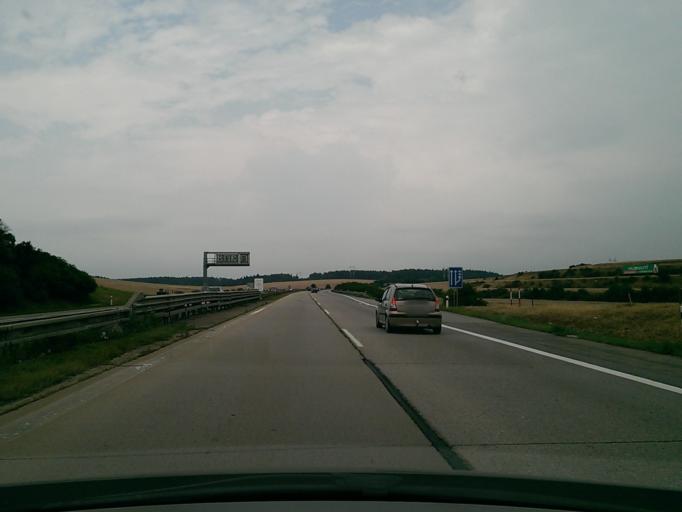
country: CZ
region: South Moravian
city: Ricany
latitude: 49.2207
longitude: 16.4000
